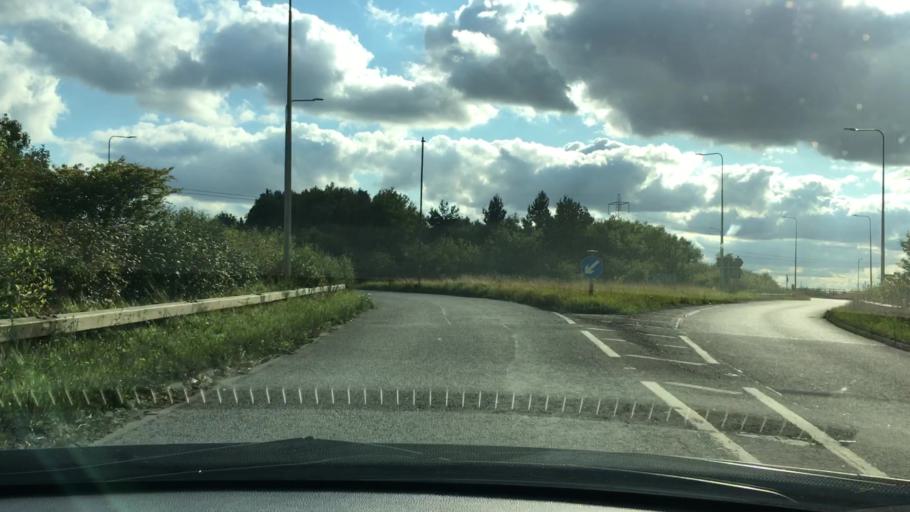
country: GB
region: England
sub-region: North East Lincolnshire
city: Immingham
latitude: 53.5987
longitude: -0.1965
